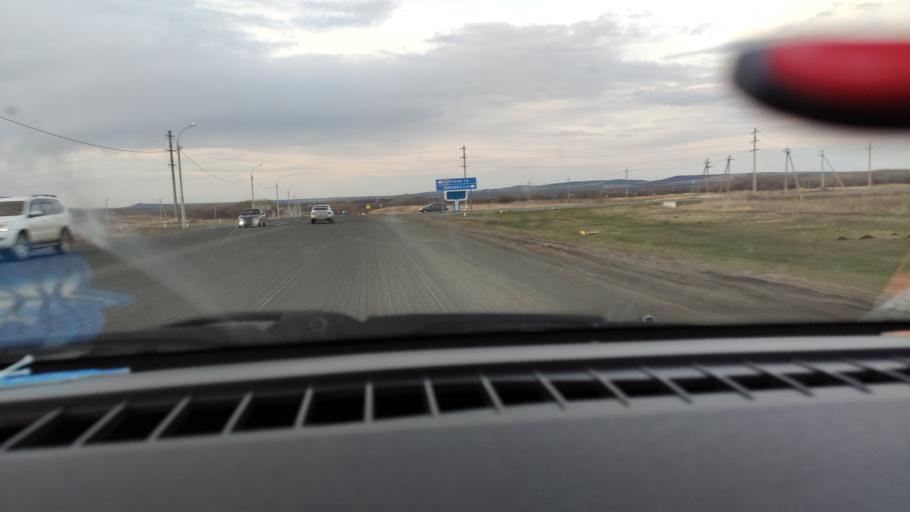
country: RU
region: Saratov
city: Yelshanka
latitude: 51.8190
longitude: 46.2139
